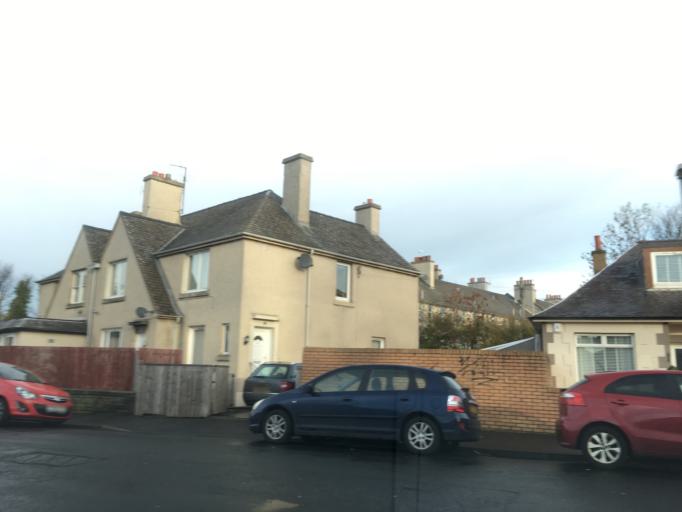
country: GB
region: Scotland
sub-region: Edinburgh
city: Colinton
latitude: 55.9321
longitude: -3.2473
